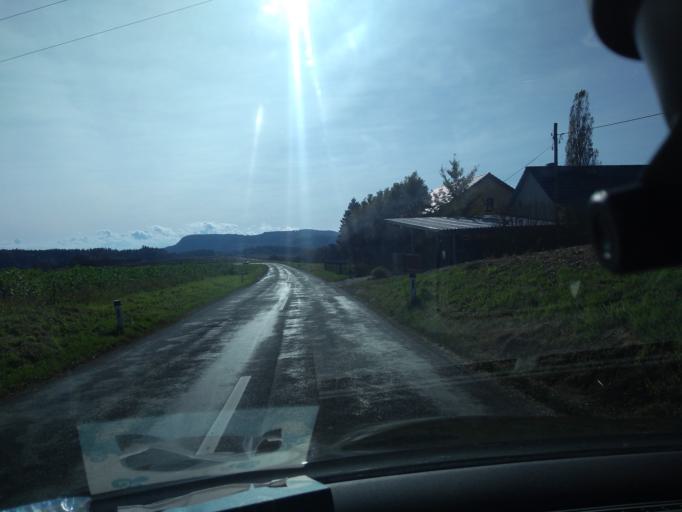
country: AT
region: Styria
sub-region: Politischer Bezirk Leibnitz
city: Sankt Ulrich am Waasen
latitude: 46.9193
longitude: 15.5313
